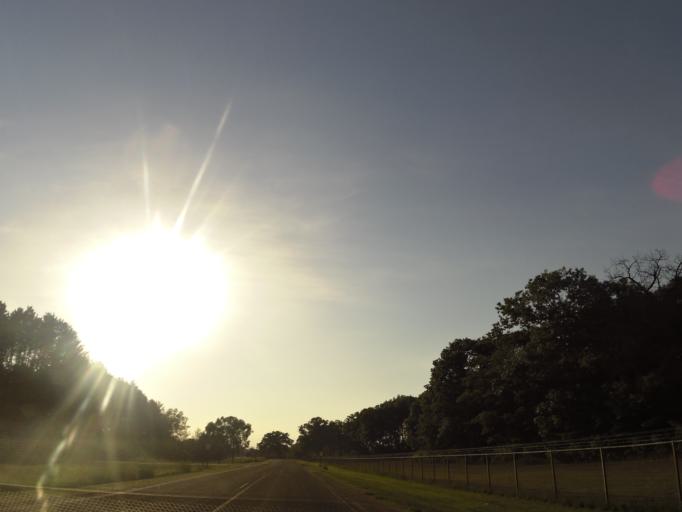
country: US
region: Wisconsin
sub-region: Juneau County
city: New Lisbon
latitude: 43.9219
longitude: -90.2587
